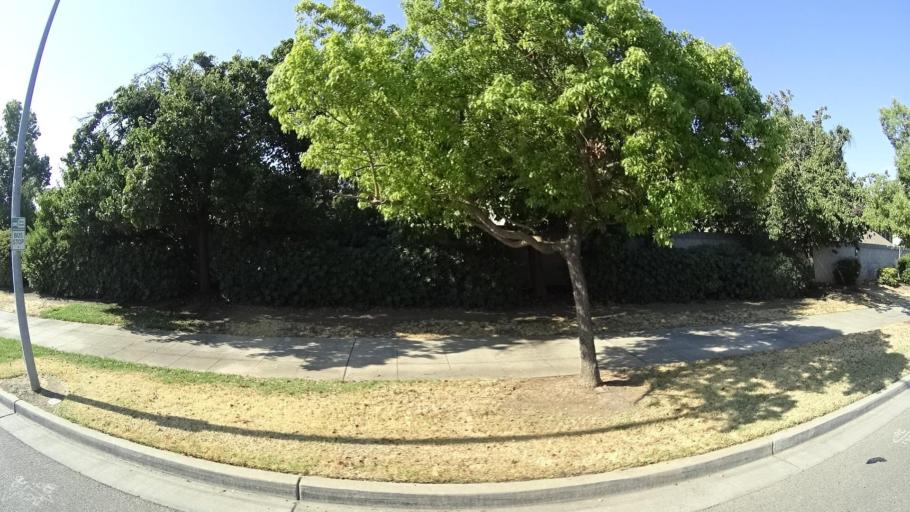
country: US
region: California
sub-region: Fresno County
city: Tarpey Village
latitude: 36.7938
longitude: -119.6556
